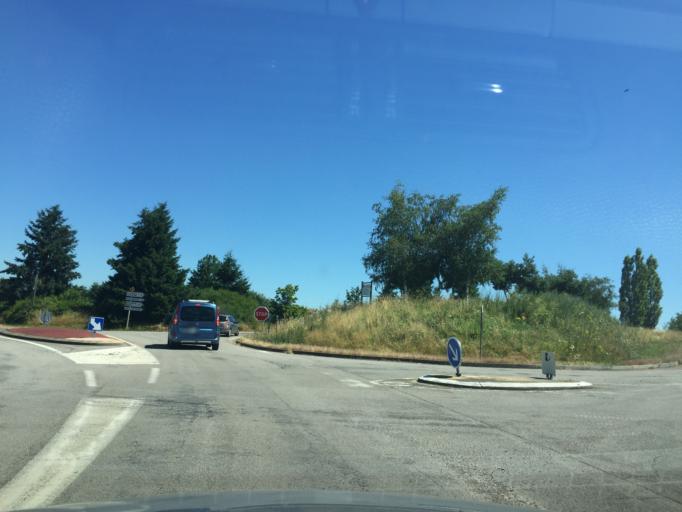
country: FR
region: Rhone-Alpes
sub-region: Departement de la Loire
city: Renaison
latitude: 46.0405
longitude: 3.9315
